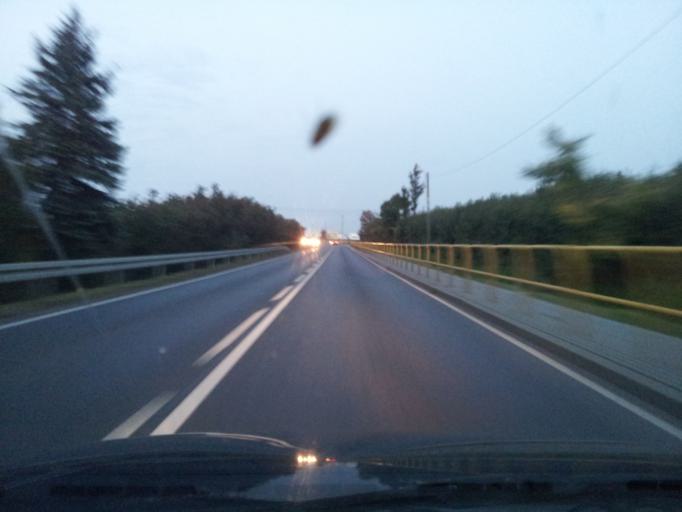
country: PL
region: Kujawsko-Pomorskie
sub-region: Powiat brodnicki
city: Brodnica
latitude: 53.2597
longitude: 19.3641
